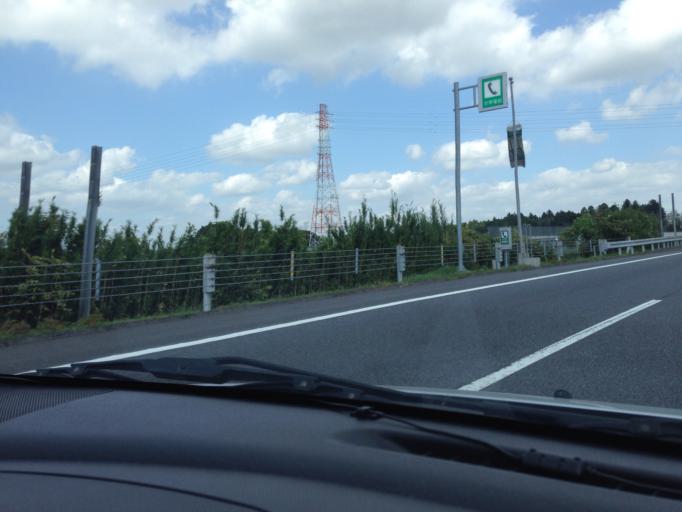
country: JP
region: Ibaraki
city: Ishioka
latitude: 36.2203
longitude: 140.2802
